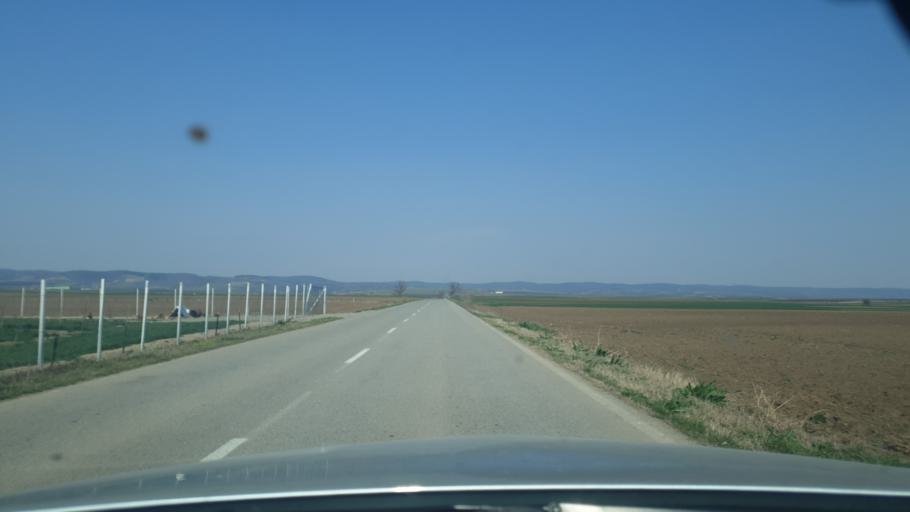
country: RS
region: Autonomna Pokrajina Vojvodina
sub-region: Sremski Okrug
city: Ruma
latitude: 45.0529
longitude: 19.7656
